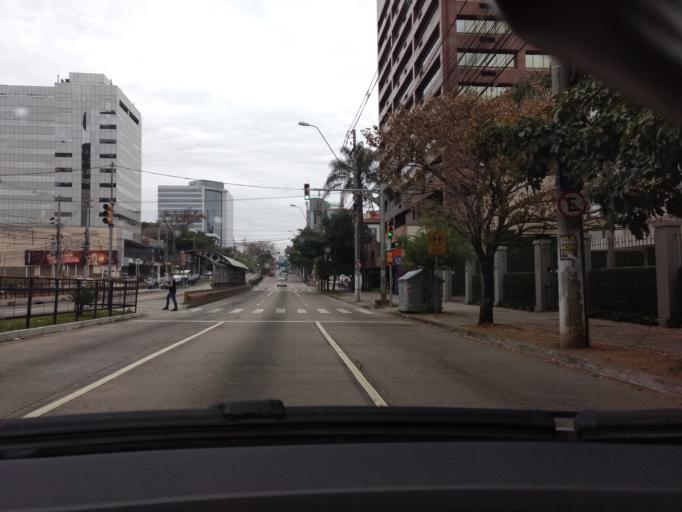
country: BR
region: Rio Grande do Sul
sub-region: Porto Alegre
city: Porto Alegre
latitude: -30.0248
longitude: -51.1832
